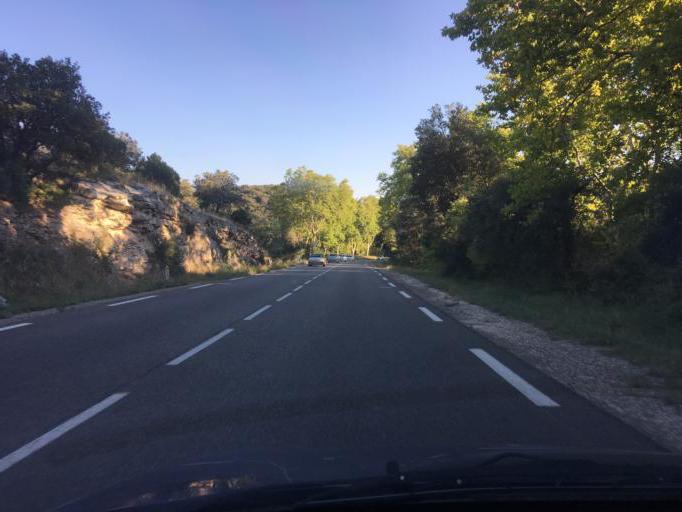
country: FR
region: Languedoc-Roussillon
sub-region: Departement du Gard
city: Castillon-du-Gard
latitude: 44.0196
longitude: 4.5817
